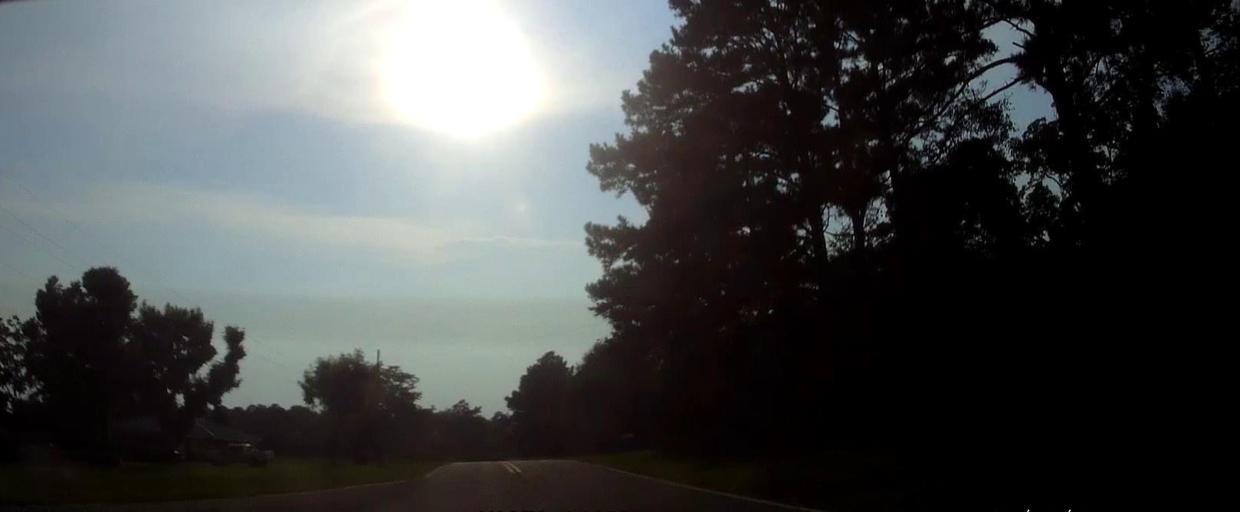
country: US
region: Georgia
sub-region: Laurens County
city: Dublin
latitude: 32.4793
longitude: -82.9550
